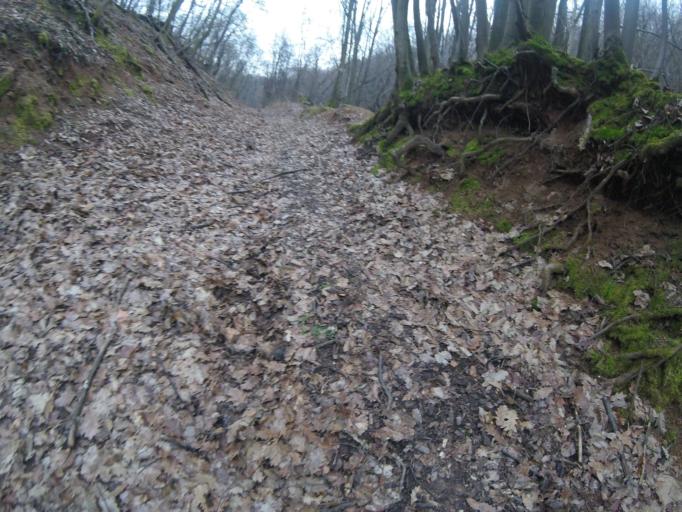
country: HU
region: Baranya
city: Mecseknadasd
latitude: 46.1418
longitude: 18.5174
